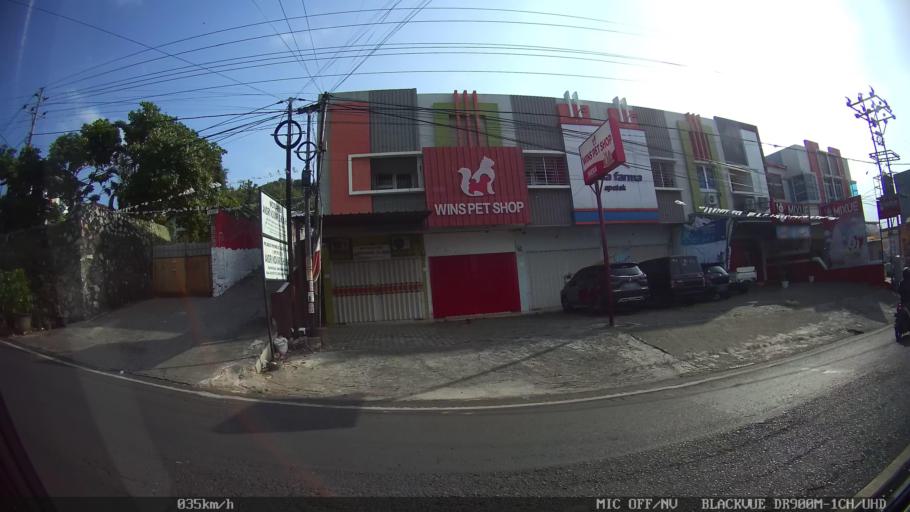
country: ID
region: Lampung
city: Bandarlampung
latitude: -5.4062
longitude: 105.2528
